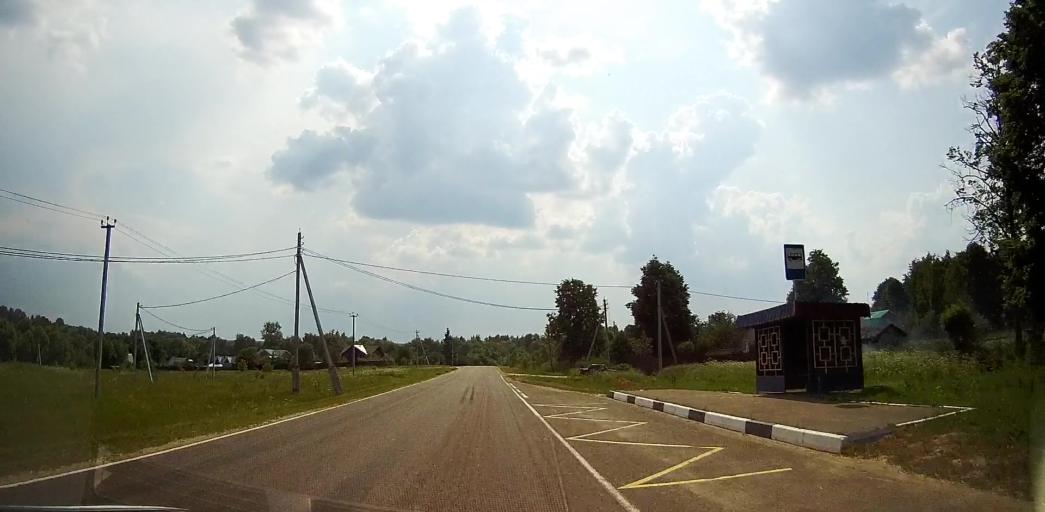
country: RU
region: Moskovskaya
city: Zhilevo
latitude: 55.0582
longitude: 38.0851
